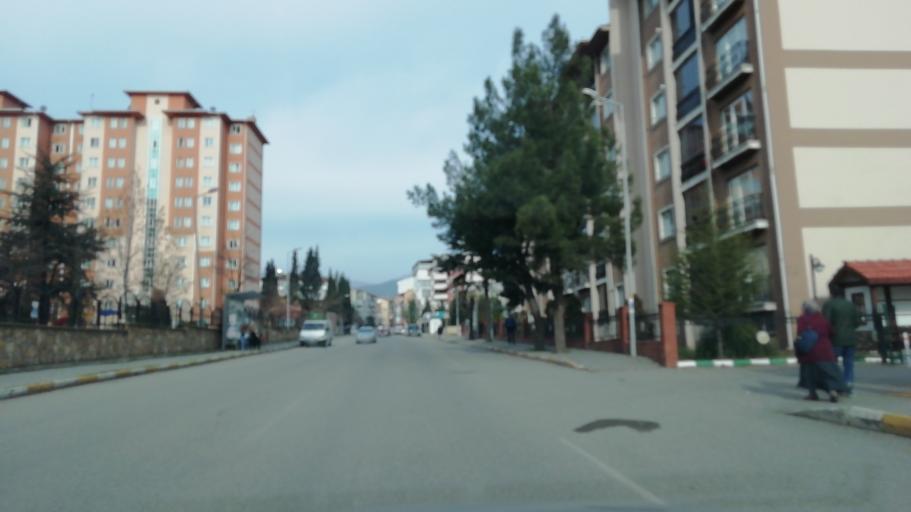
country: TR
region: Karabuk
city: Karabuk
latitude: 41.2020
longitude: 32.6264
